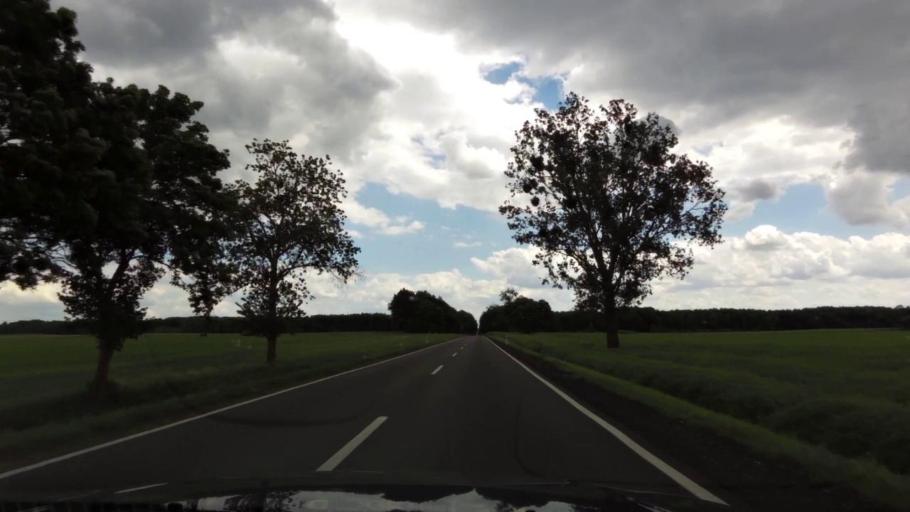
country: PL
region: West Pomeranian Voivodeship
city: Trzcinsko Zdroj
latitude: 52.9757
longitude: 14.7255
